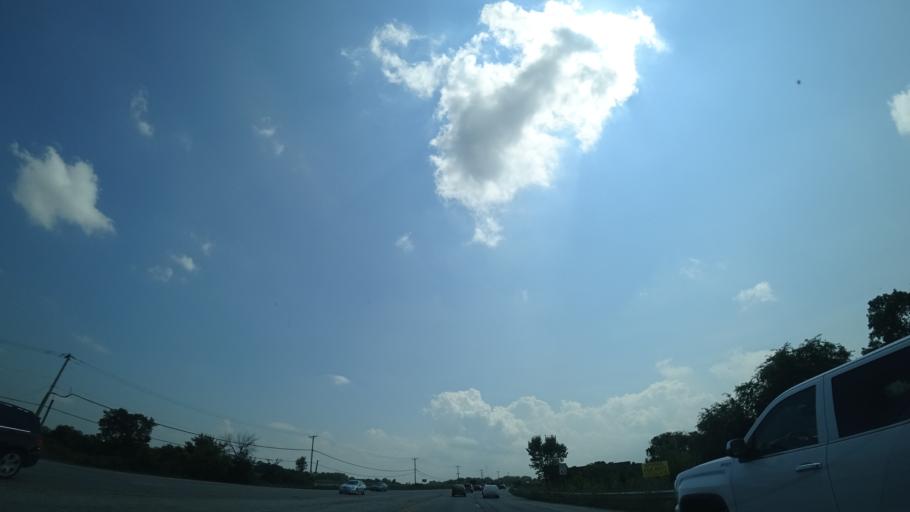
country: US
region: Illinois
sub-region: Will County
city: Frankfort Square
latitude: 41.5397
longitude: -87.7908
